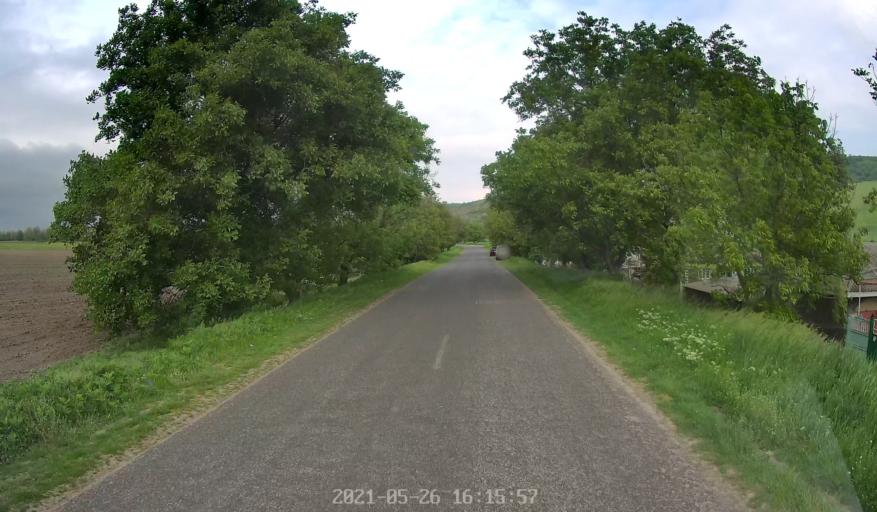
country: MD
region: Hincesti
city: Dancu
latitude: 46.7199
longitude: 28.3519
